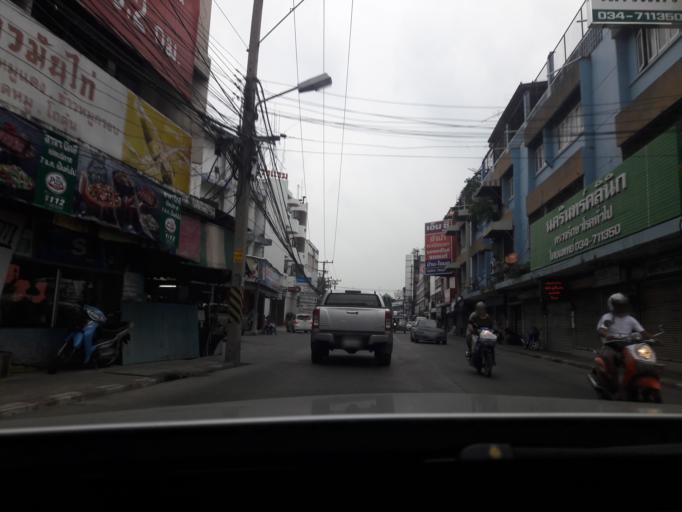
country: TH
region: Samut Songkhram
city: Samut Songkhram
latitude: 13.4083
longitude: 100.0016
